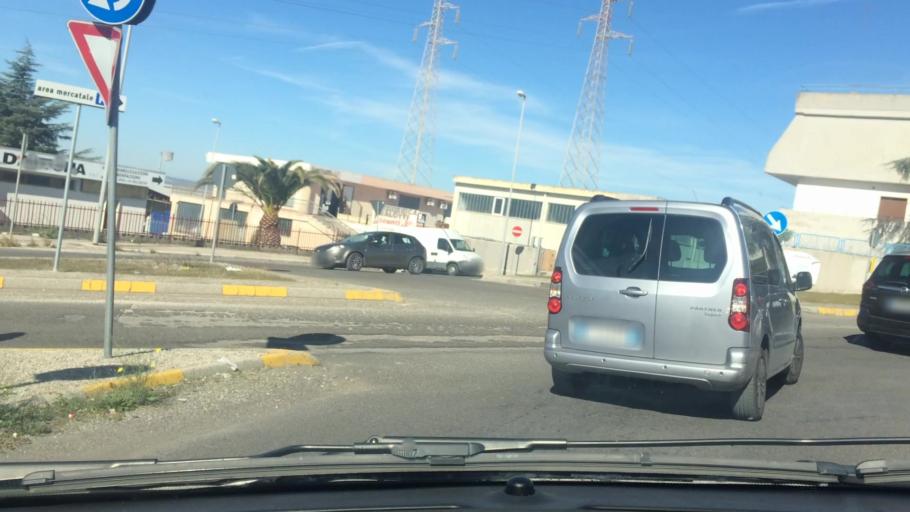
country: IT
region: Basilicate
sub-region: Provincia di Matera
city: Matera
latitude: 40.6734
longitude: 16.5761
